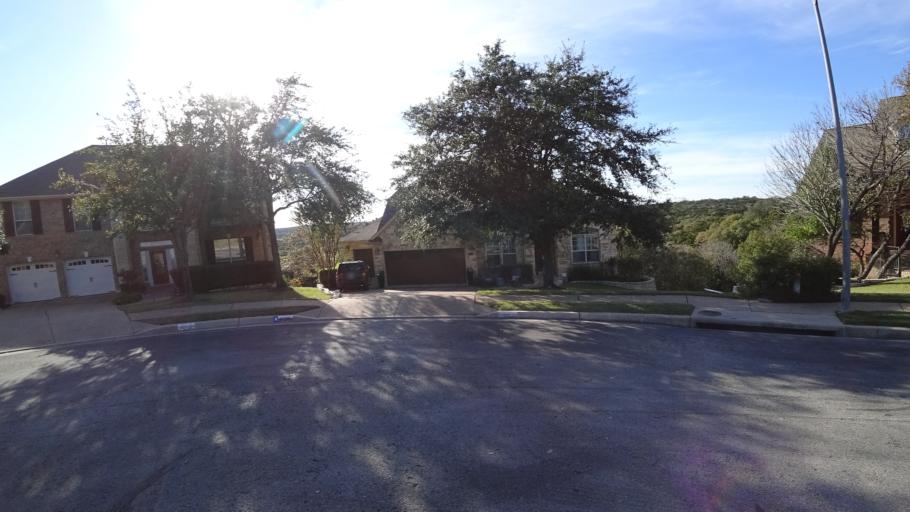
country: US
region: Texas
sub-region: Williamson County
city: Jollyville
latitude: 30.4071
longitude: -97.7775
